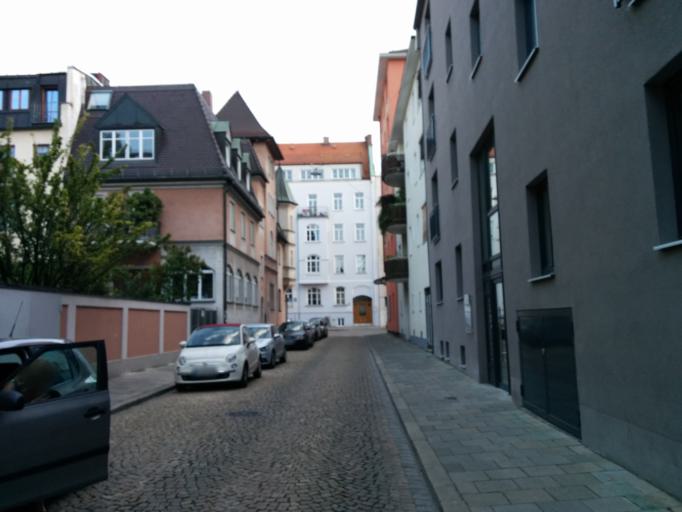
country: DE
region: Bavaria
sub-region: Upper Bavaria
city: Munich
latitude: 48.1596
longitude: 11.5862
